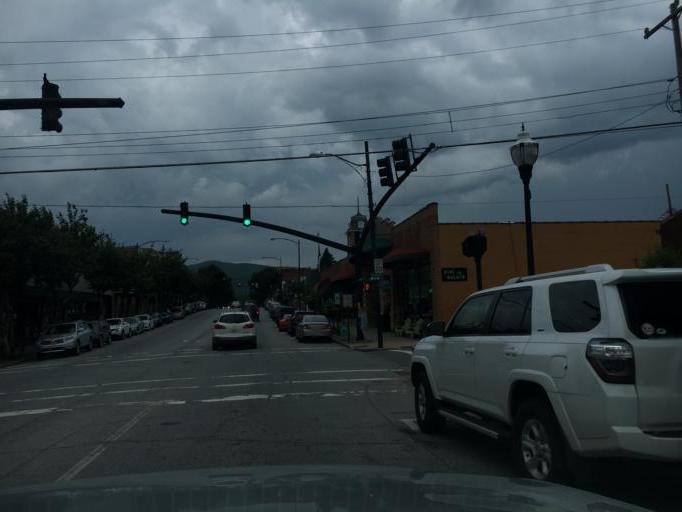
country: US
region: North Carolina
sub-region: Transylvania County
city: Brevard
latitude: 35.2331
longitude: -82.7329
